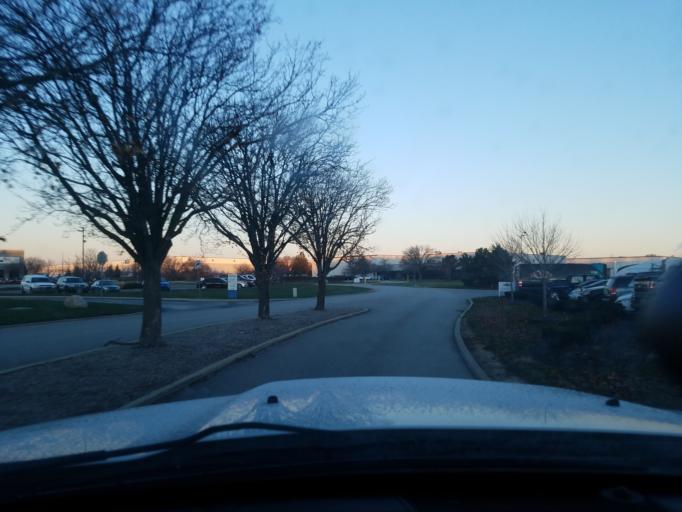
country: US
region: Indiana
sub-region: Boone County
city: Zionsville
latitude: 39.8935
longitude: -86.2424
